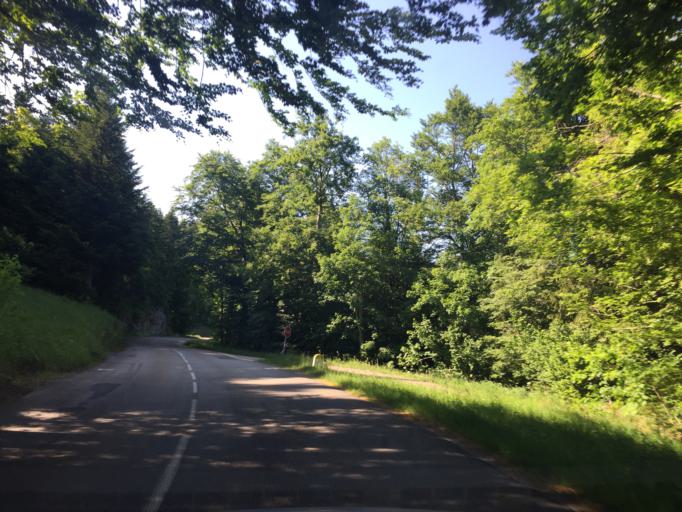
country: FR
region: Rhone-Alpes
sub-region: Departement de la Drome
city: Saint-Jean-en-Royans
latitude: 44.9582
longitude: 5.3306
